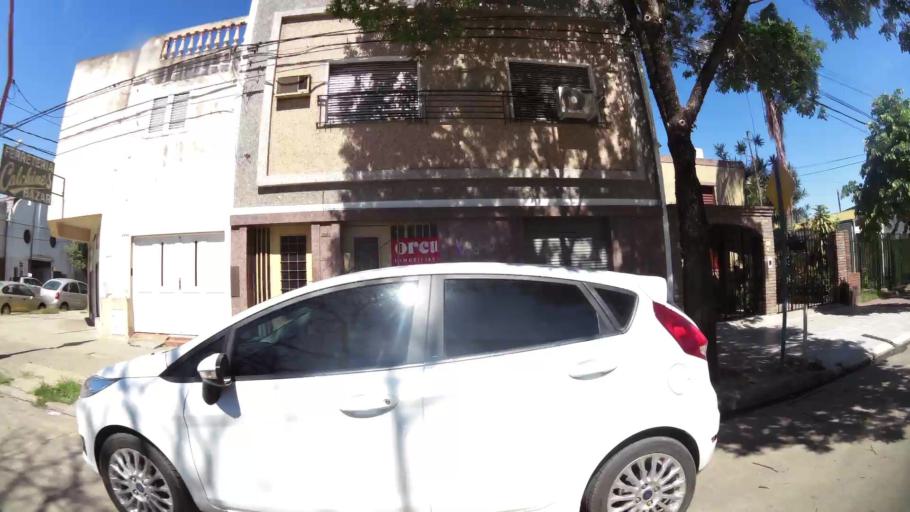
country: AR
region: Santa Fe
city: Santa Fe de la Vera Cruz
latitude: -31.6423
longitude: -60.6958
